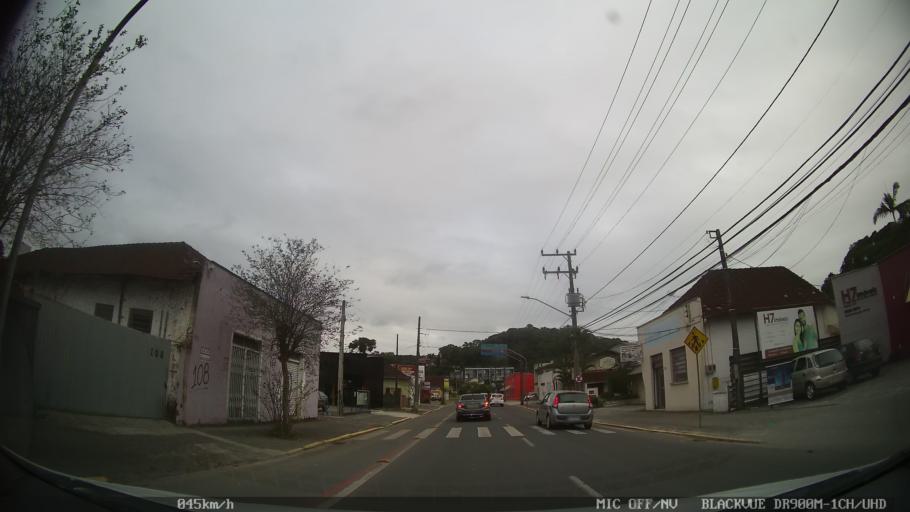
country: BR
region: Santa Catarina
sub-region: Joinville
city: Joinville
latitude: -26.2950
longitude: -48.8682
